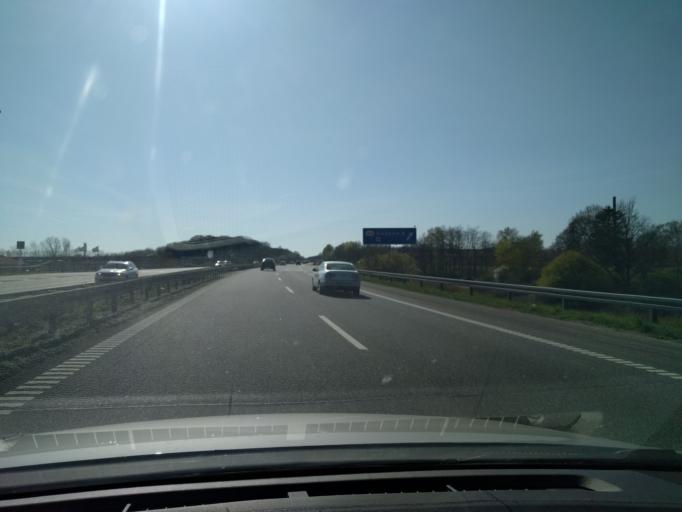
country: DK
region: Zealand
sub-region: Slagelse Kommune
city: Slagelse
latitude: 55.3920
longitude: 11.3604
